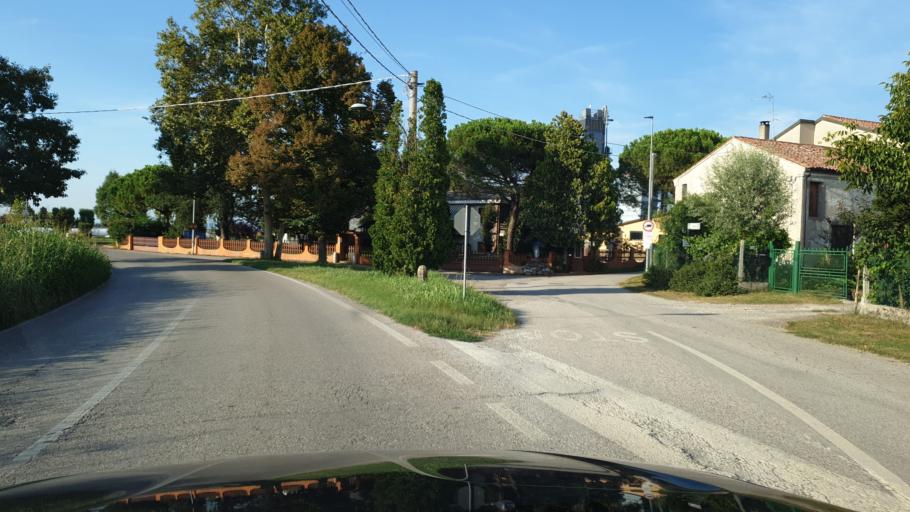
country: IT
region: Veneto
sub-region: Provincia di Rovigo
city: Fiesso Umbertiano
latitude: 44.9697
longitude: 11.6112
